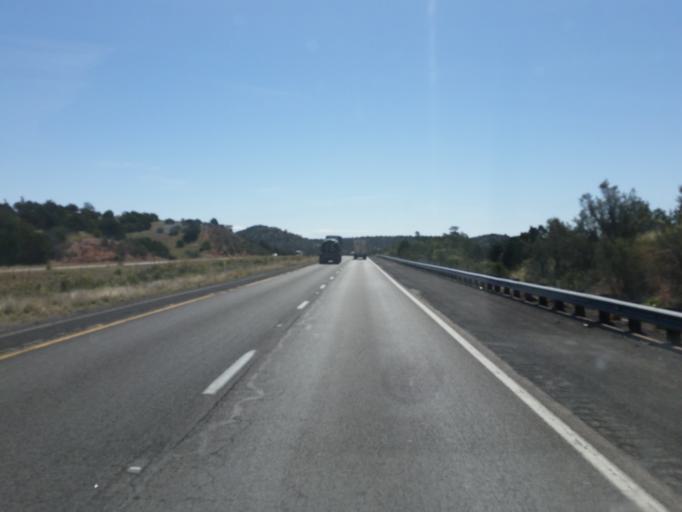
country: US
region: Arizona
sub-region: Mohave County
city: Peach Springs
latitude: 35.2921
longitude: -113.0431
